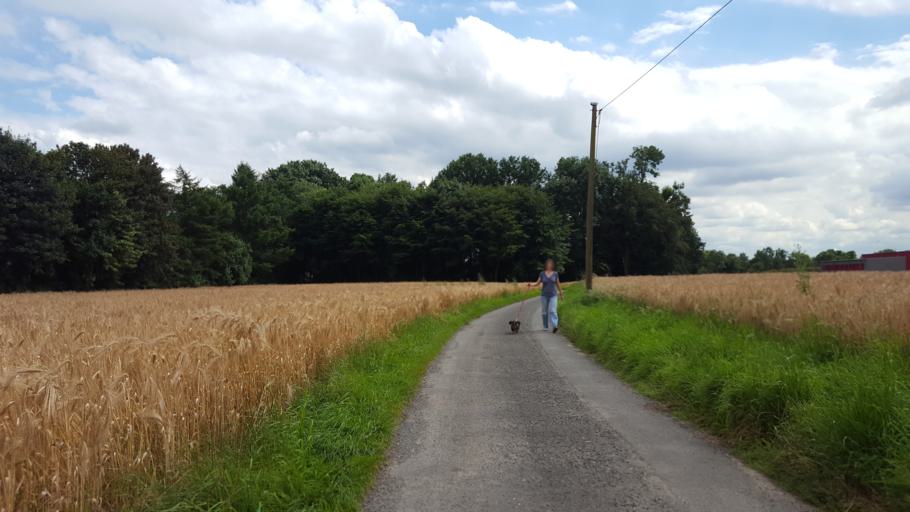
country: DE
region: North Rhine-Westphalia
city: Oer-Erkenschwick
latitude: 51.6407
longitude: 7.2850
